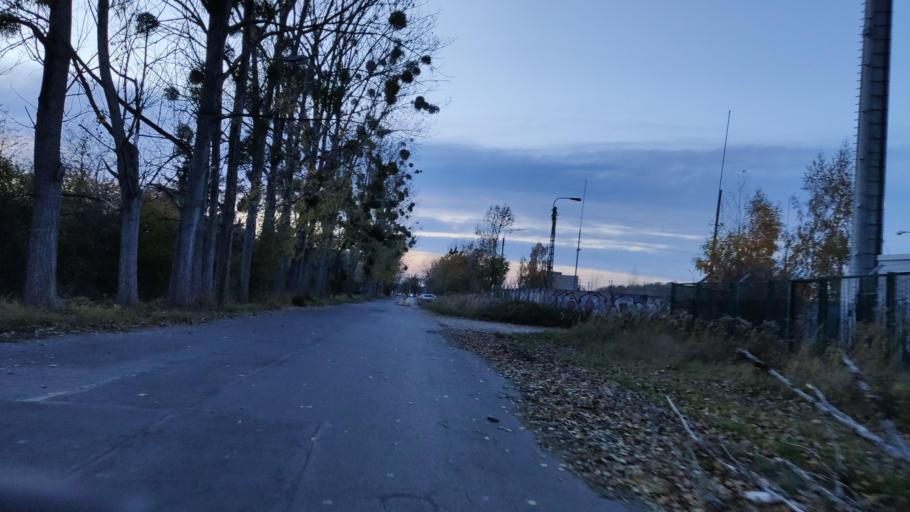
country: PL
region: Lower Silesian Voivodeship
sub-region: Powiat wroclawski
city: Zerniki Wroclawskie
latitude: 51.0687
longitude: 17.0594
